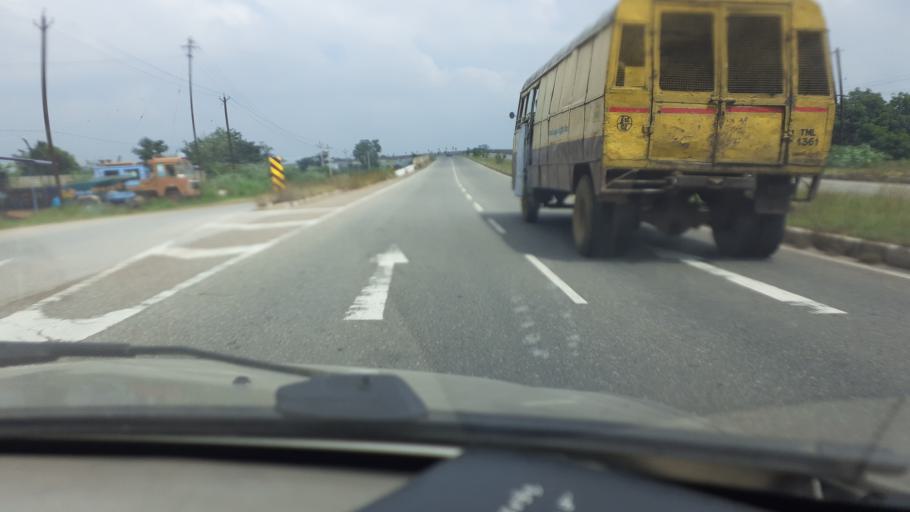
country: IN
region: Tamil Nadu
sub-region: Tirunelveli Kattabo
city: Nanguneri
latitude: 8.4764
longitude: 77.6594
